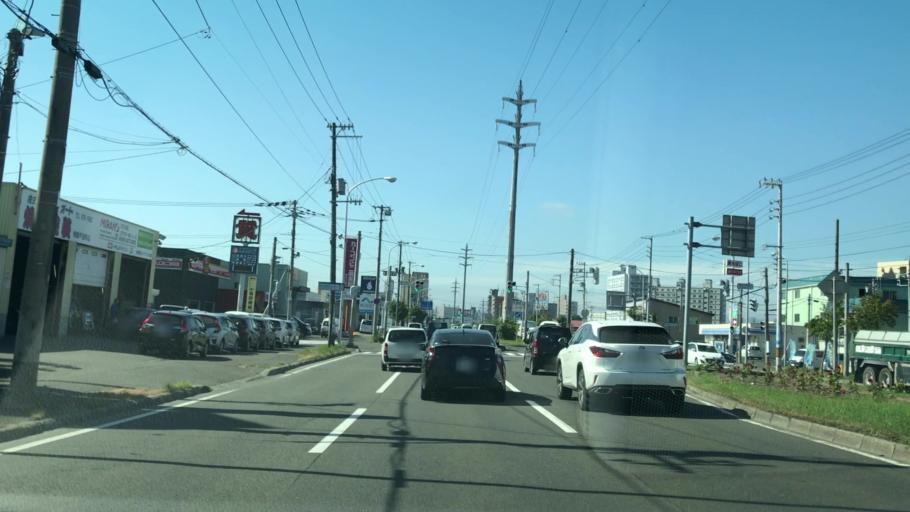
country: JP
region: Hokkaido
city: Sapporo
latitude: 43.0703
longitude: 141.4089
